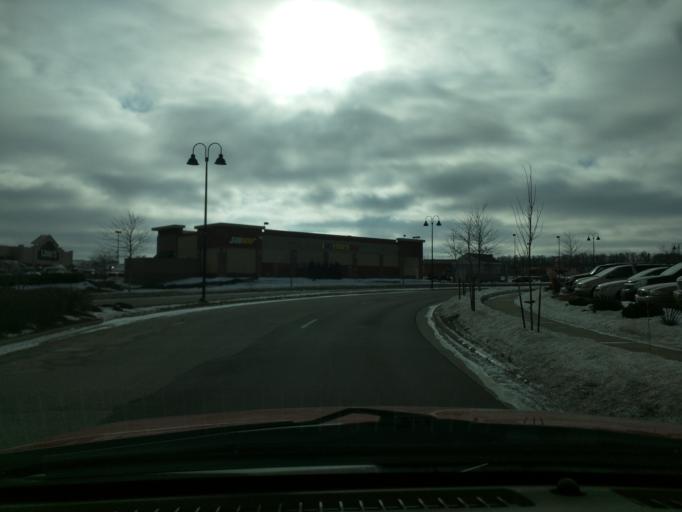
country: US
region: Minnesota
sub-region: Olmsted County
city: Rochester
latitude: 43.9564
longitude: -92.4614
